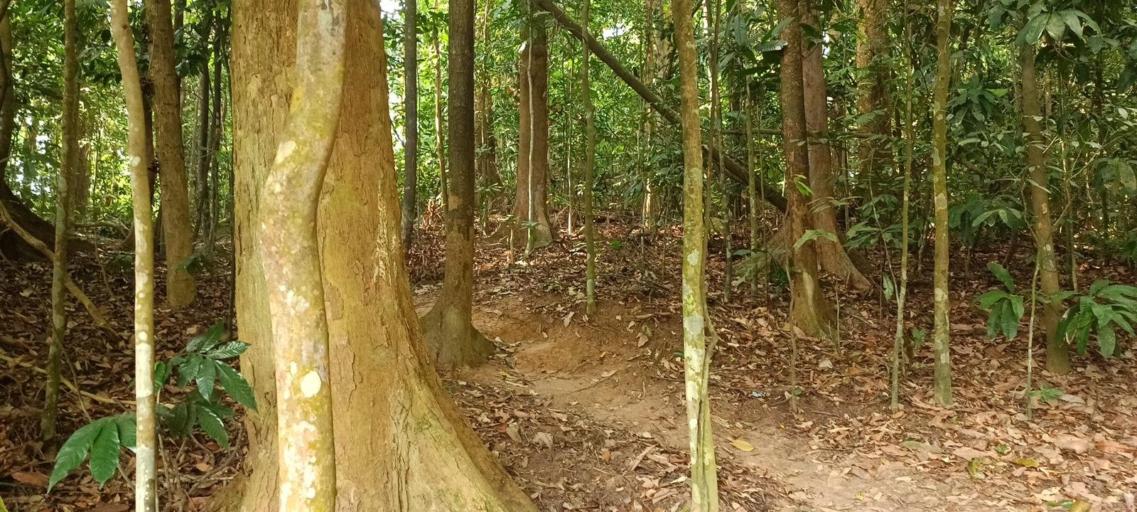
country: MY
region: Penang
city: Juru
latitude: 5.3318
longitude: 100.4128
